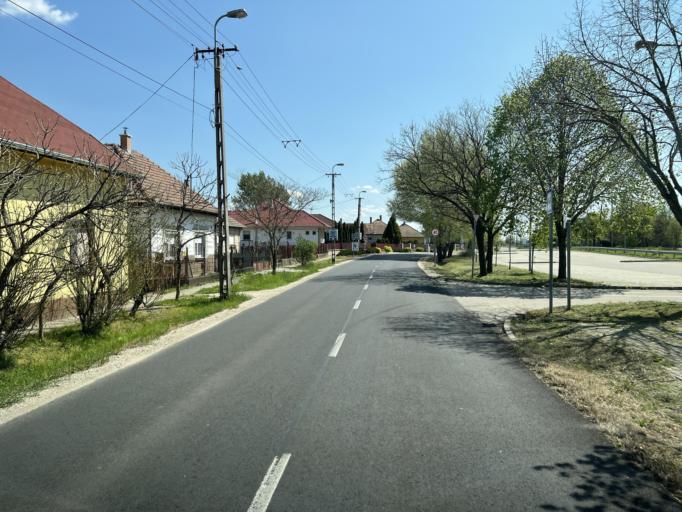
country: HU
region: Pest
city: Inarcs
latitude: 47.2467
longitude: 19.3190
